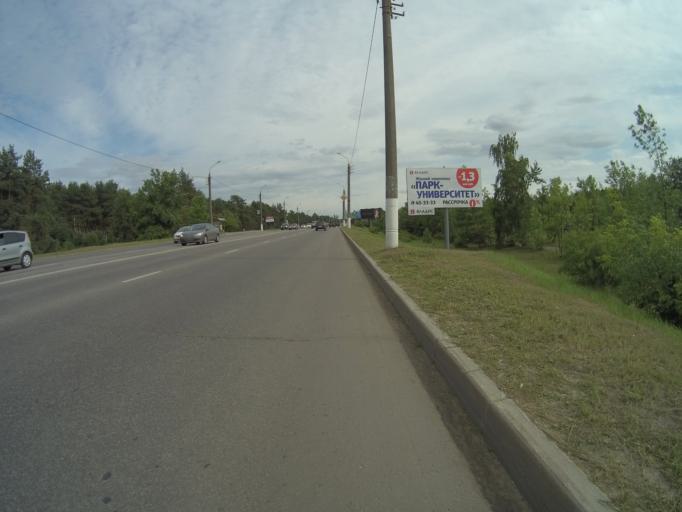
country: RU
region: Vladimir
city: Kommunar
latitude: 56.1065
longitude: 40.4334
